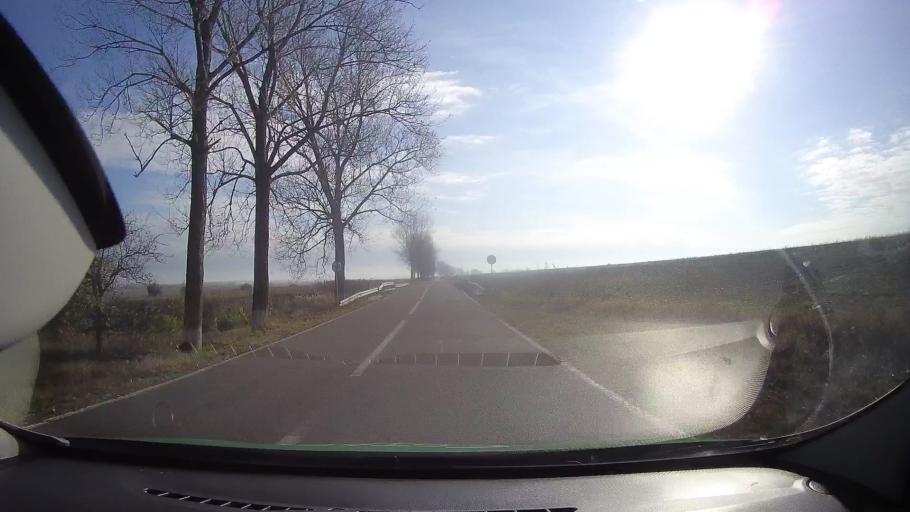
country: RO
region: Tulcea
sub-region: Comuna Mahmudia
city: Mahmudia
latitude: 45.0694
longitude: 29.0997
